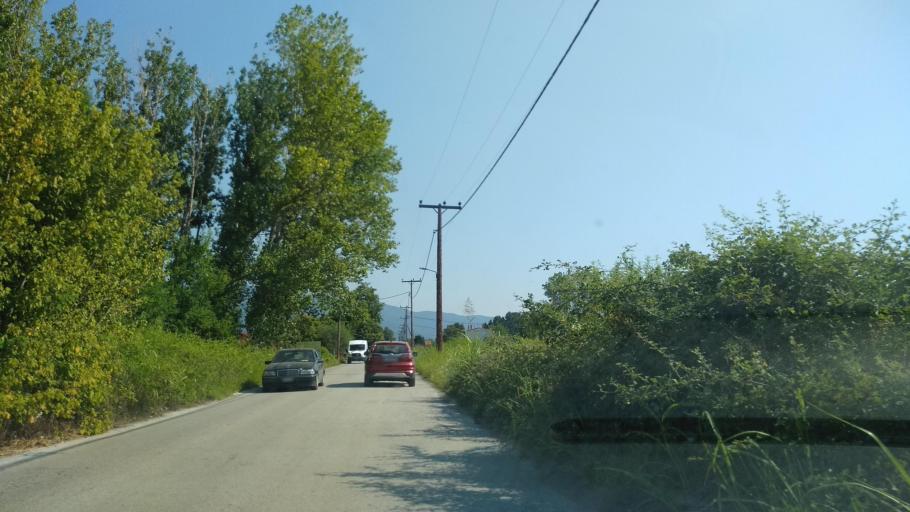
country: GR
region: Central Macedonia
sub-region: Nomos Thessalonikis
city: Stavros
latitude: 40.6807
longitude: 23.6870
